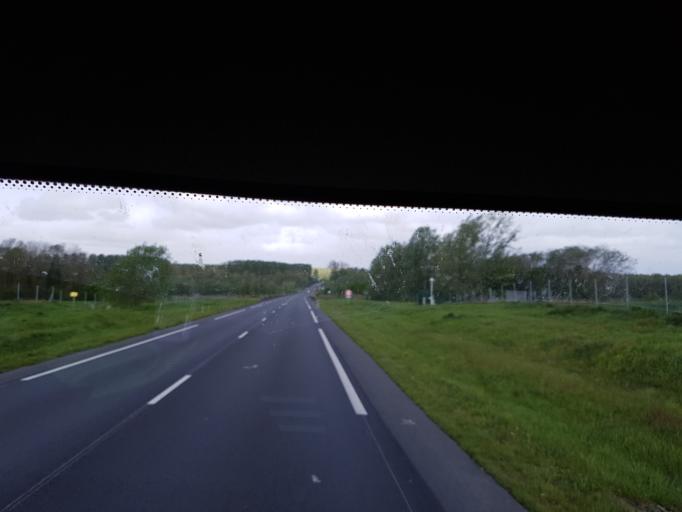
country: FR
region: Nord-Pas-de-Calais
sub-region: Departement du Nord
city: Proville
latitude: 50.1541
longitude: 3.1929
